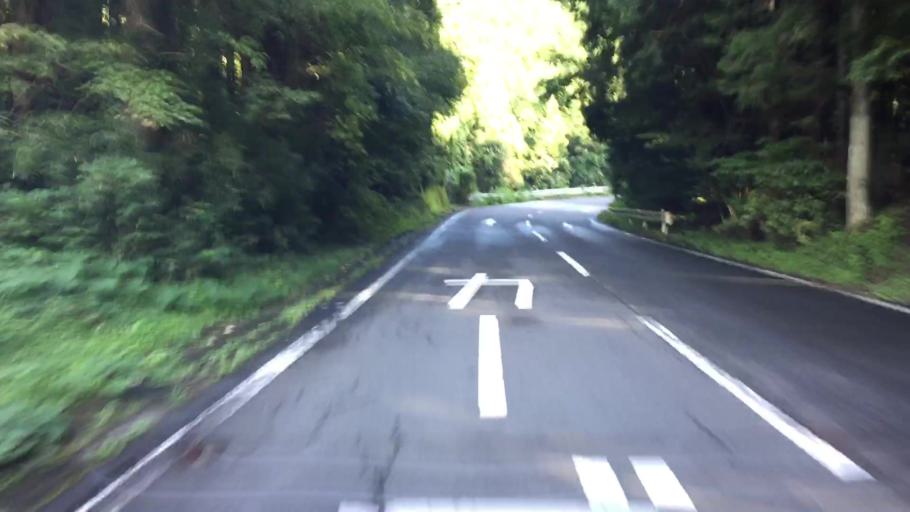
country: JP
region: Tochigi
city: Imaichi
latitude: 36.7582
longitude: 139.6838
